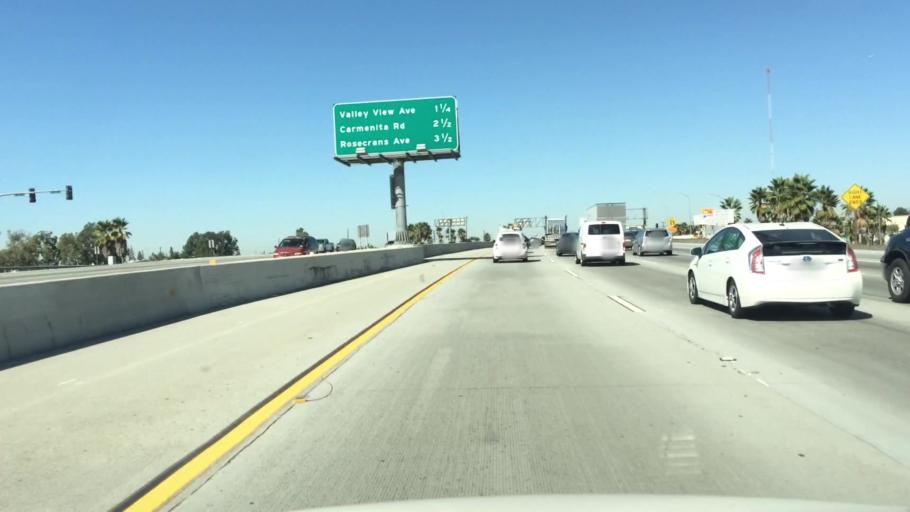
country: US
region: California
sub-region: Orange County
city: Buena Park
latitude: 33.8715
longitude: -118.0073
